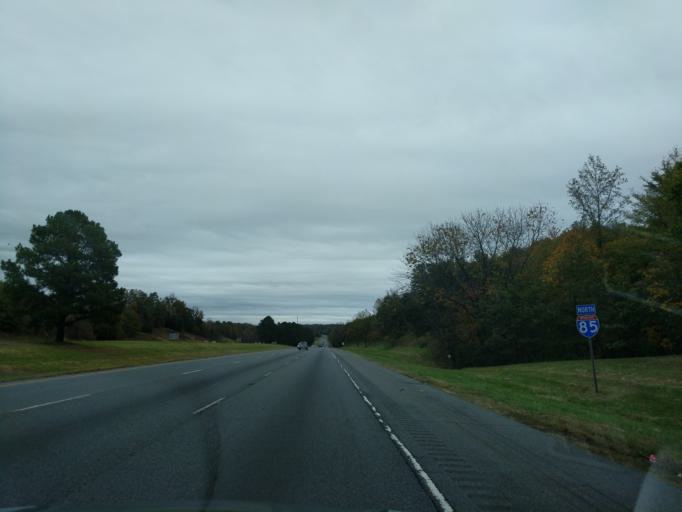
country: US
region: North Carolina
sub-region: Davidson County
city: Lexington
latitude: 35.7823
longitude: -80.2520
